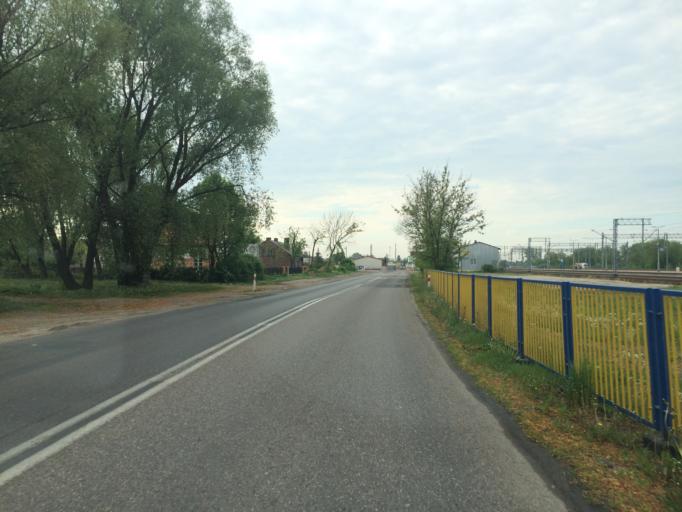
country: PL
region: Masovian Voivodeship
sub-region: Powiat mlawski
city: Mlawa
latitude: 53.1261
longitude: 20.3518
